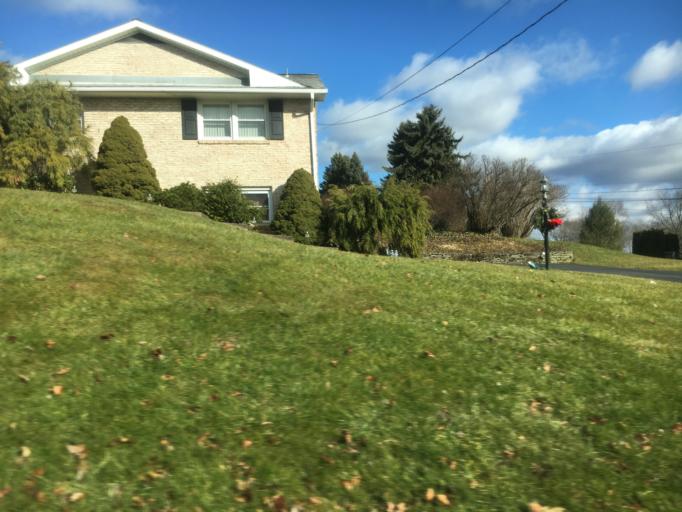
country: US
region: Pennsylvania
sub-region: Lehigh County
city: Egypt
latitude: 40.6845
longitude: -75.5437
